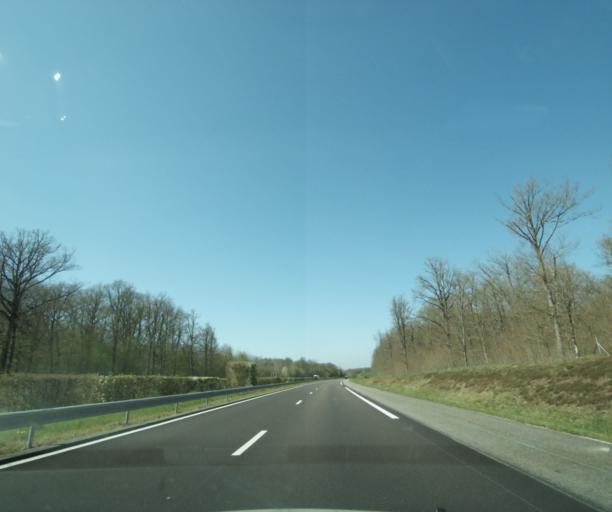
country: FR
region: Bourgogne
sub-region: Departement de la Nievre
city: Neuvy-sur-Loire
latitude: 47.5006
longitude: 2.9259
